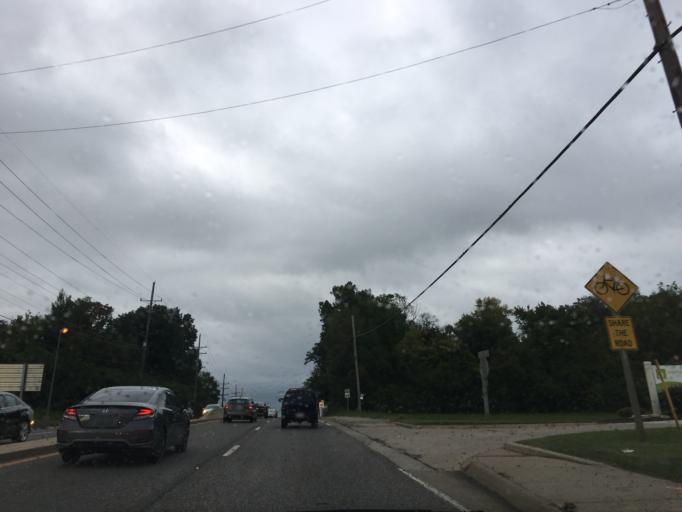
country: US
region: Missouri
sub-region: Saint Louis County
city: Saint Ann
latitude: 38.7238
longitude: -90.4068
